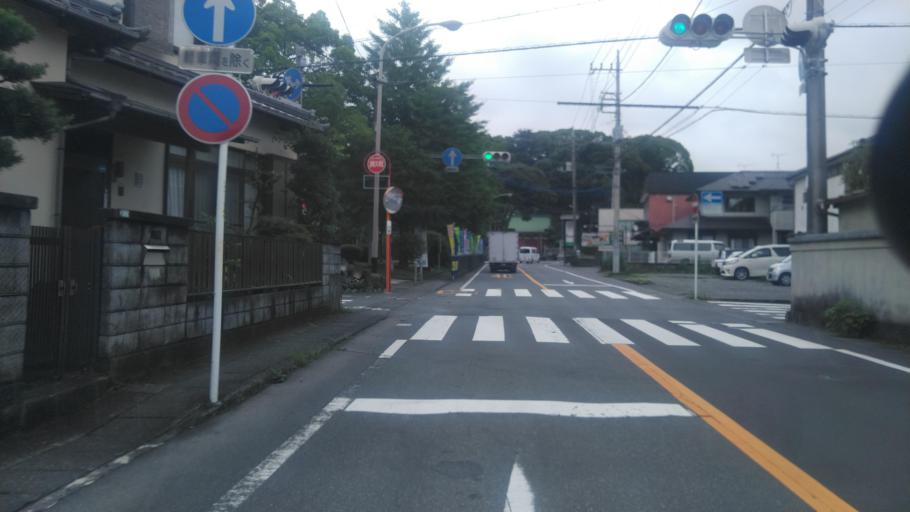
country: JP
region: Shizuoka
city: Fujinomiya
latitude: 35.2284
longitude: 138.6156
